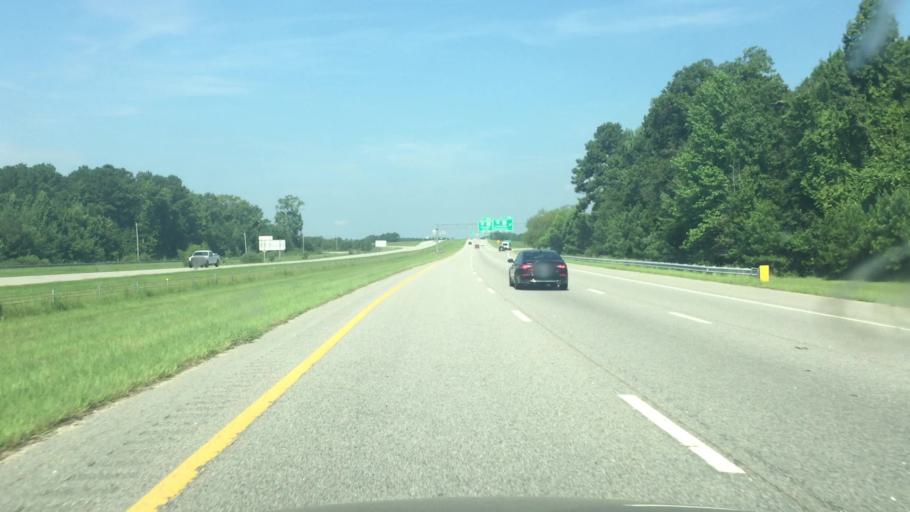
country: US
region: North Carolina
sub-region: Robeson County
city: Lumberton
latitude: 34.5916
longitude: -79.1003
